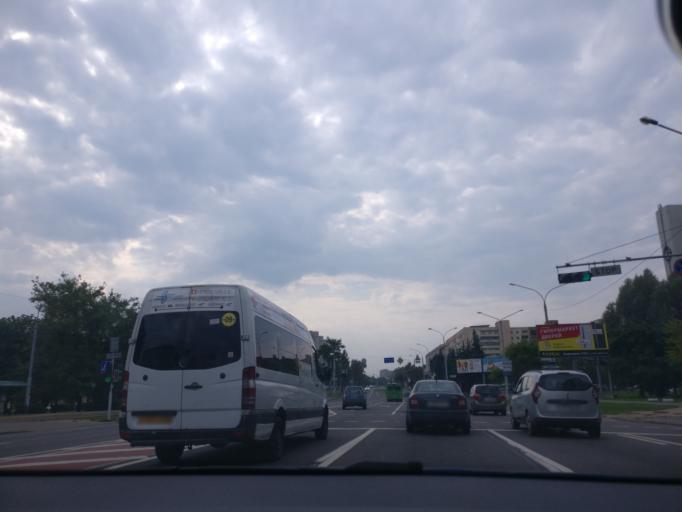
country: BY
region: Minsk
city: Minsk
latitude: 53.9397
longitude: 27.6062
